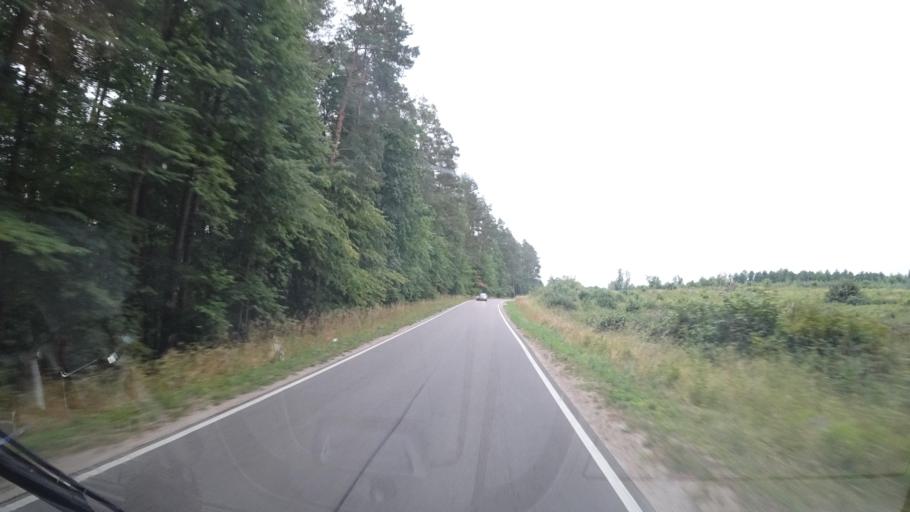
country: PL
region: Warmian-Masurian Voivodeship
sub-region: Powiat gizycki
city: Ryn
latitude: 53.8817
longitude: 21.5806
